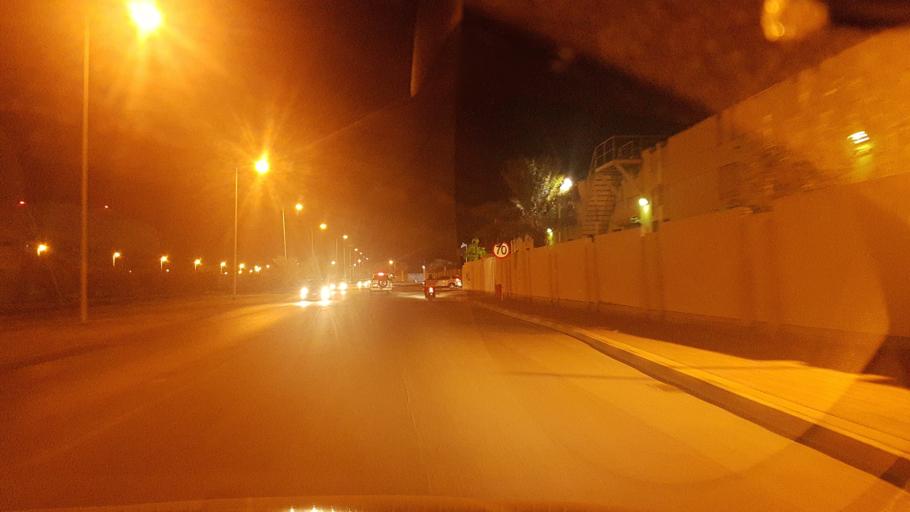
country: BH
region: Muharraq
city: Al Muharraq
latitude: 26.2799
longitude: 50.6299
